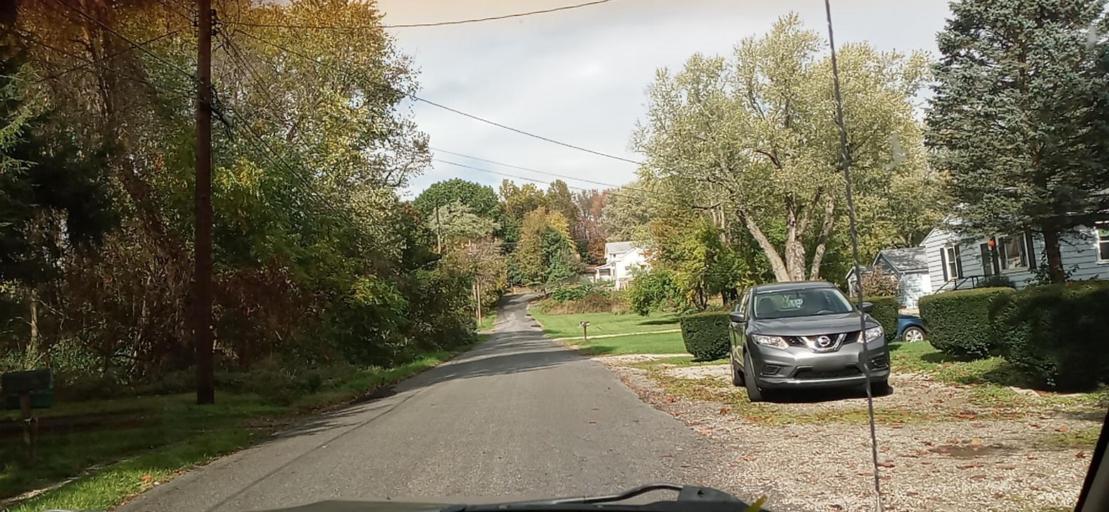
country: US
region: Ohio
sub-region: Summit County
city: Portage Lakes
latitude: 41.0138
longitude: -81.4897
